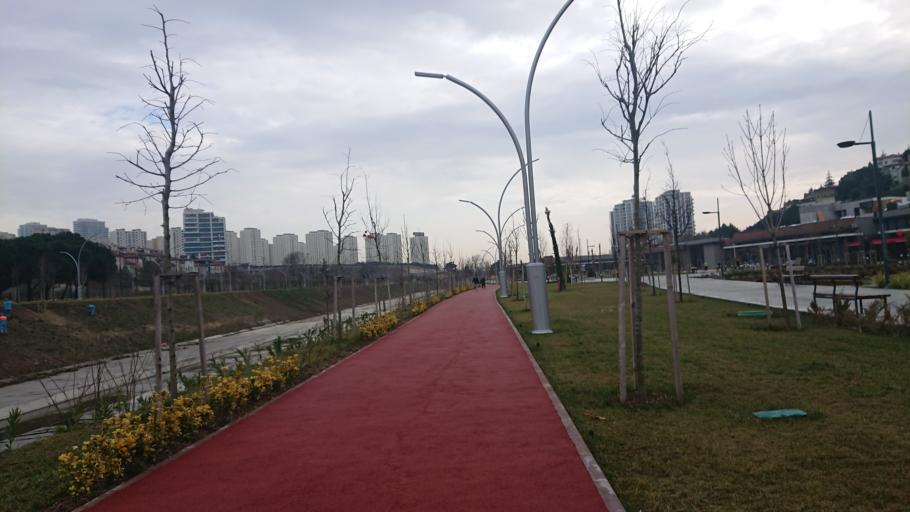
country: TR
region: Istanbul
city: Esenyurt
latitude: 41.0668
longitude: 28.6954
